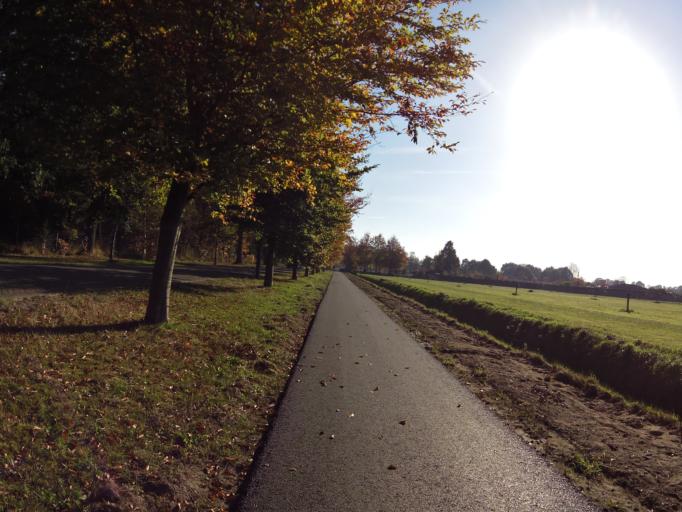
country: NL
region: North Brabant
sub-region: Gemeente Vught
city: Vught
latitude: 51.6285
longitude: 5.2818
